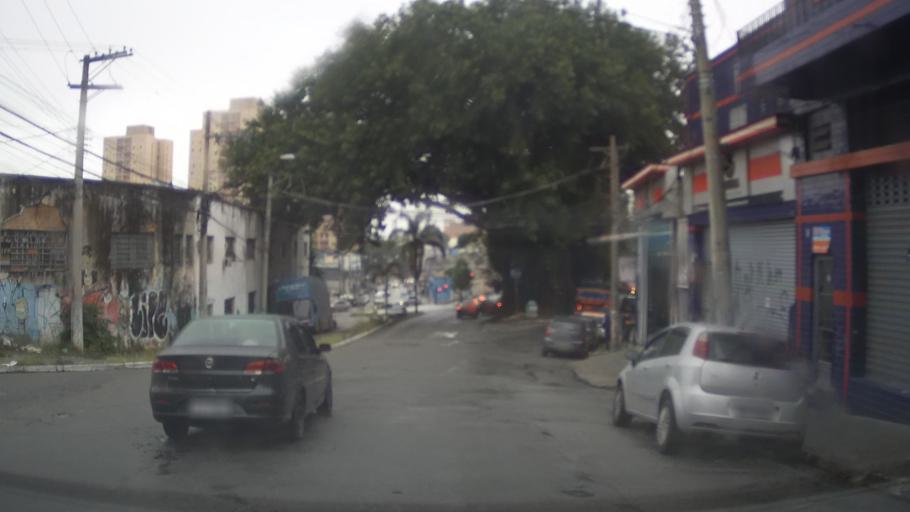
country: BR
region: Sao Paulo
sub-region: Guarulhos
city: Guarulhos
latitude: -23.4744
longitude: -46.5338
